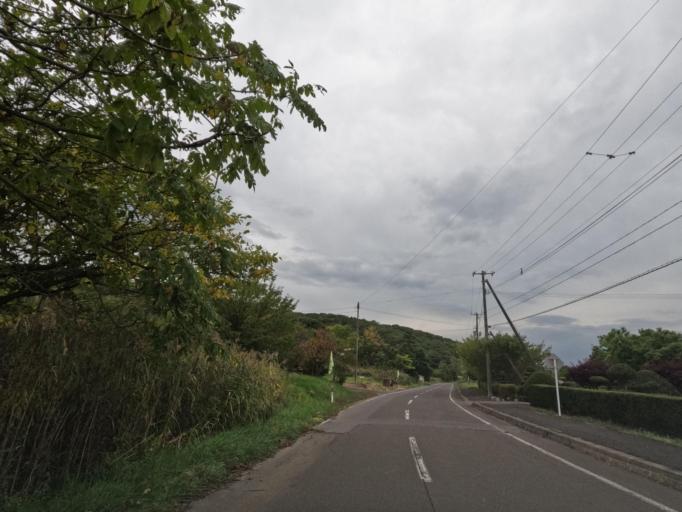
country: JP
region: Hokkaido
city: Date
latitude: 42.3987
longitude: 140.9226
